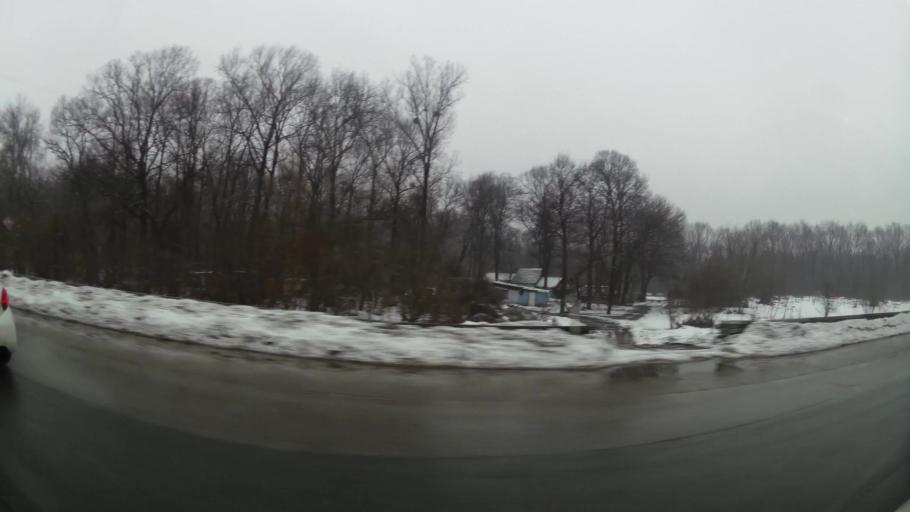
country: RS
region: Central Serbia
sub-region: Belgrade
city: Cukarica
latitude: 44.7758
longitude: 20.3998
